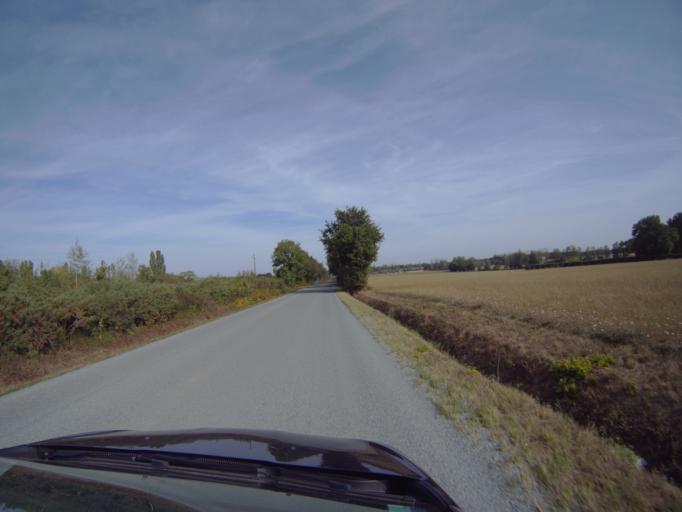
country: FR
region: Pays de la Loire
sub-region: Departement de la Vendee
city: Saint-Andre-Treize-Voies
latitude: 46.9257
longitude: -1.3985
